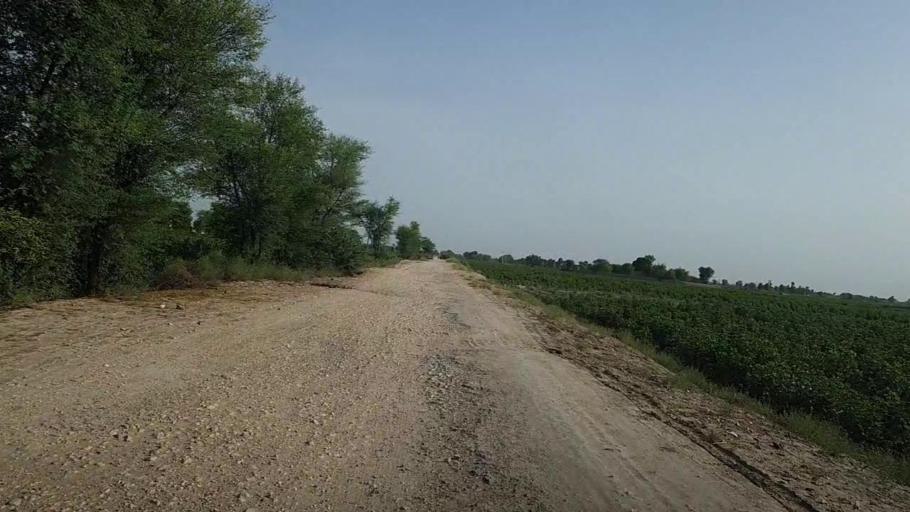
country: PK
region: Sindh
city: Pad Idan
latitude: 26.7632
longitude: 68.2572
